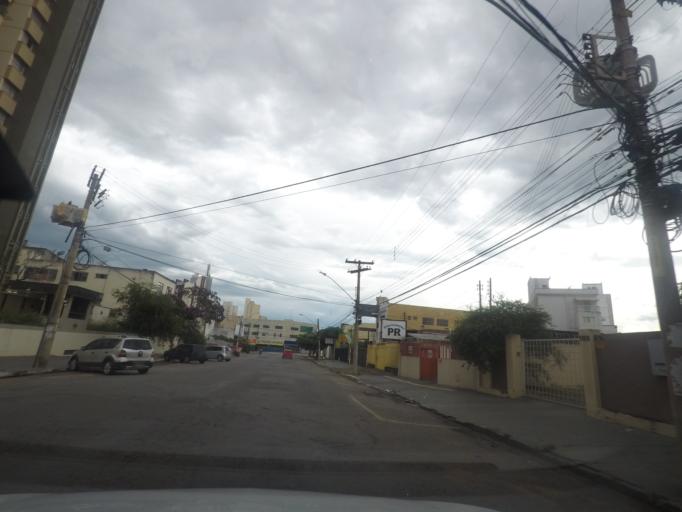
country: BR
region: Goias
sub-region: Goiania
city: Goiania
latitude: -16.6867
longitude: -49.2607
